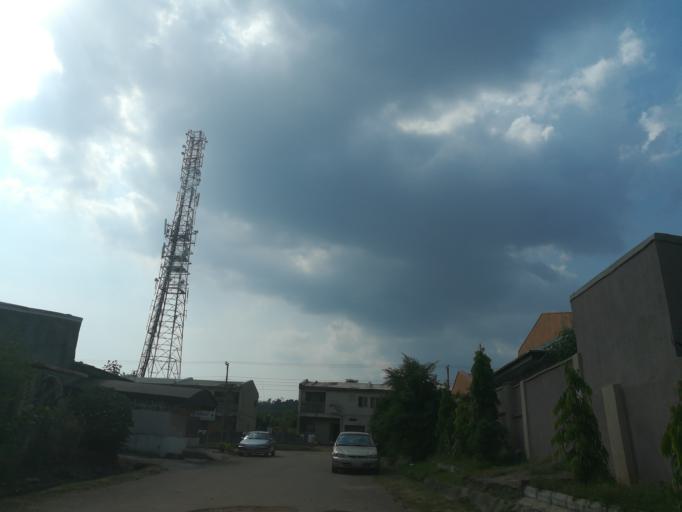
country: NG
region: Abuja Federal Capital Territory
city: Abuja
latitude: 9.0801
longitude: 7.4125
